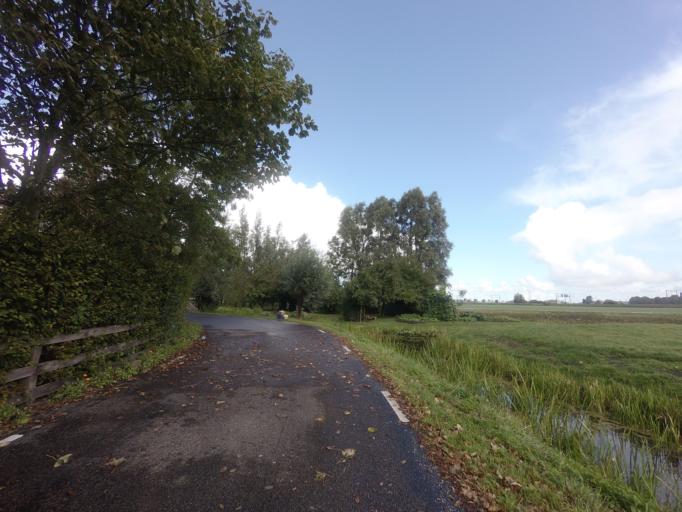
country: NL
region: Friesland
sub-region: Gemeente Leeuwarden
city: Wirdum
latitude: 53.1465
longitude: 5.7908
